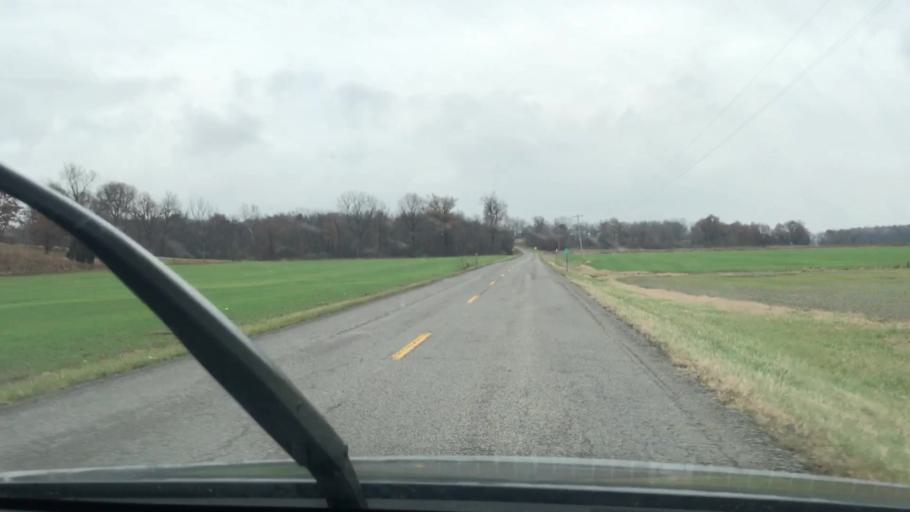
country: US
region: Kentucky
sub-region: McLean County
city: Calhoun
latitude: 37.5162
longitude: -87.3979
